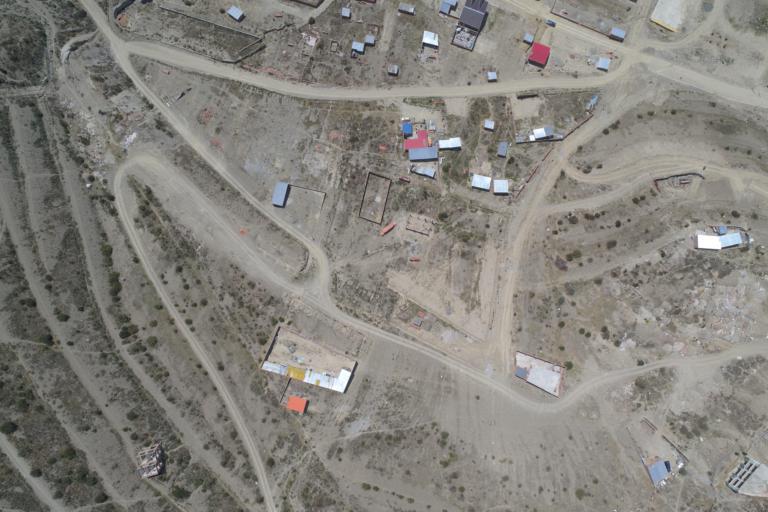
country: BO
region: La Paz
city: La Paz
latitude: -16.5038
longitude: -68.0978
